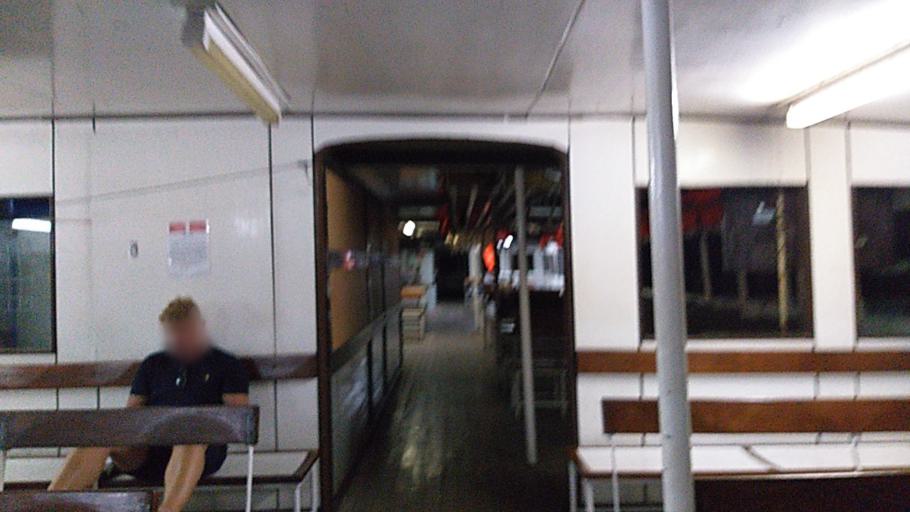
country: TH
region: Trat
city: Laem Ngop
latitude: 12.1768
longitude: 102.2990
